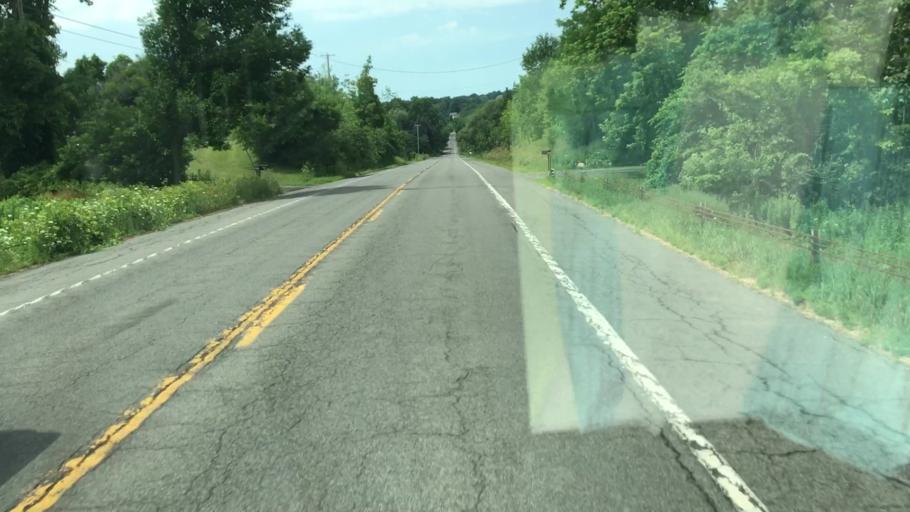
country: US
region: New York
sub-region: Onondaga County
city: Nedrow
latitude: 42.9128
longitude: -76.2298
